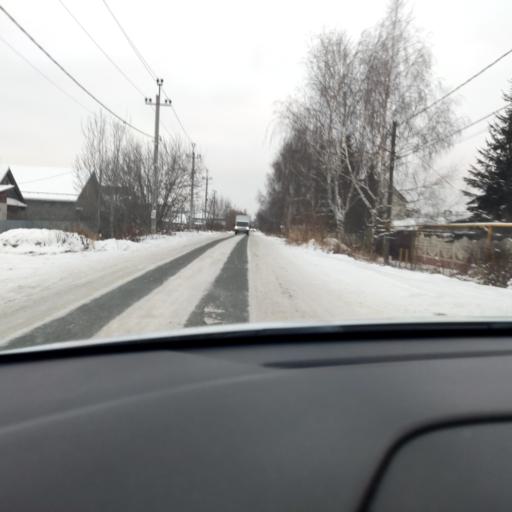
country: RU
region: Tatarstan
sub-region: Gorod Kazan'
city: Kazan
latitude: 55.8727
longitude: 49.1499
